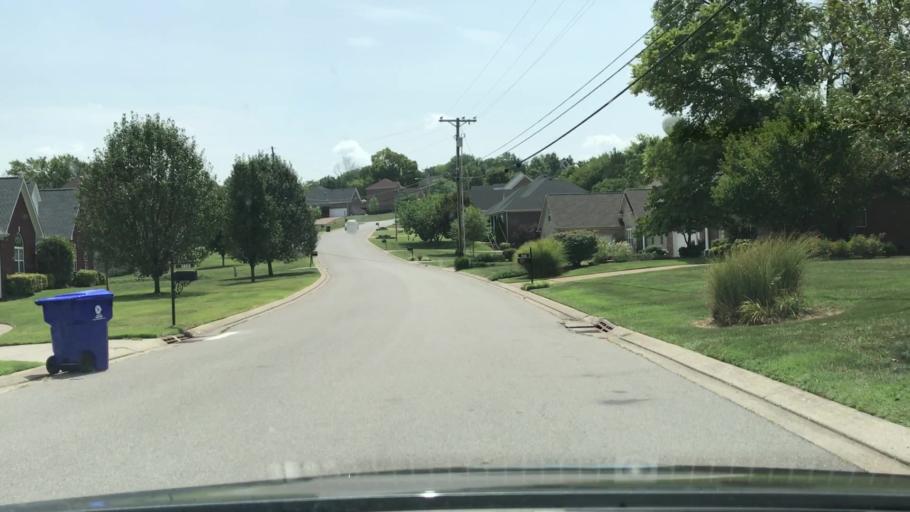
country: US
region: Tennessee
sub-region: Williamson County
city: Nolensville
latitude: 35.9641
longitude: -86.6144
